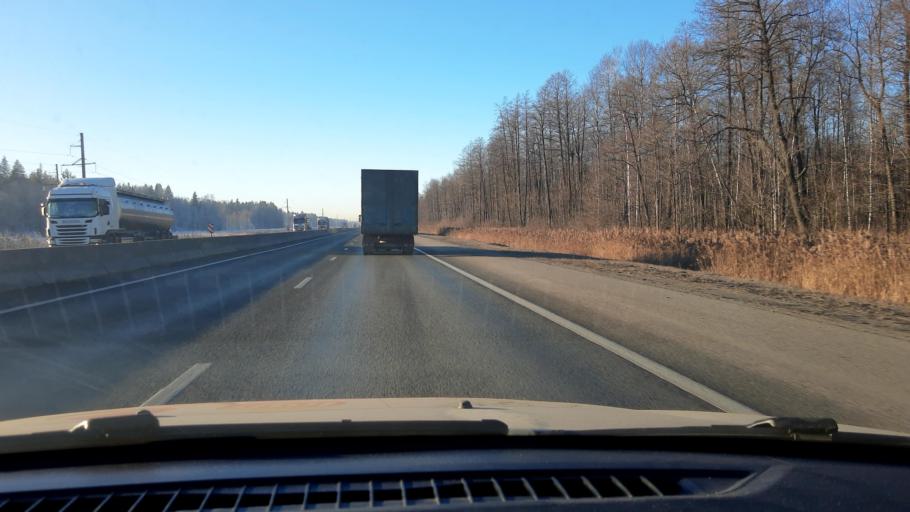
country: RU
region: Nizjnij Novgorod
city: Volodarsk
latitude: 56.2861
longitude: 43.1856
